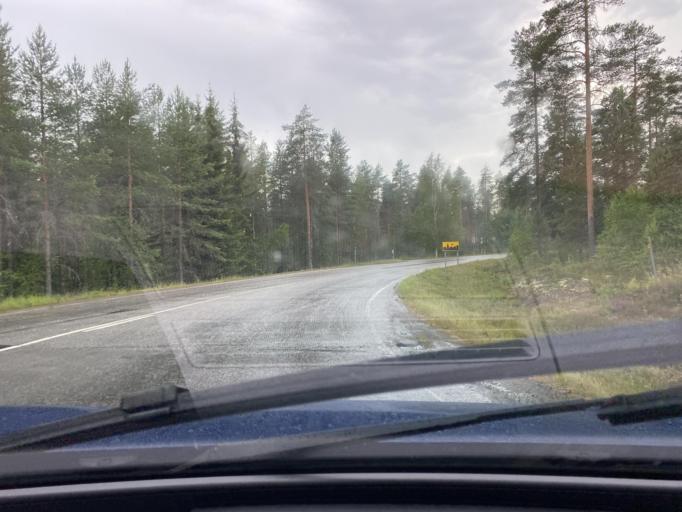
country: FI
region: Central Ostrobothnia
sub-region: Kaustinen
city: Veteli
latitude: 63.4682
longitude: 23.8296
